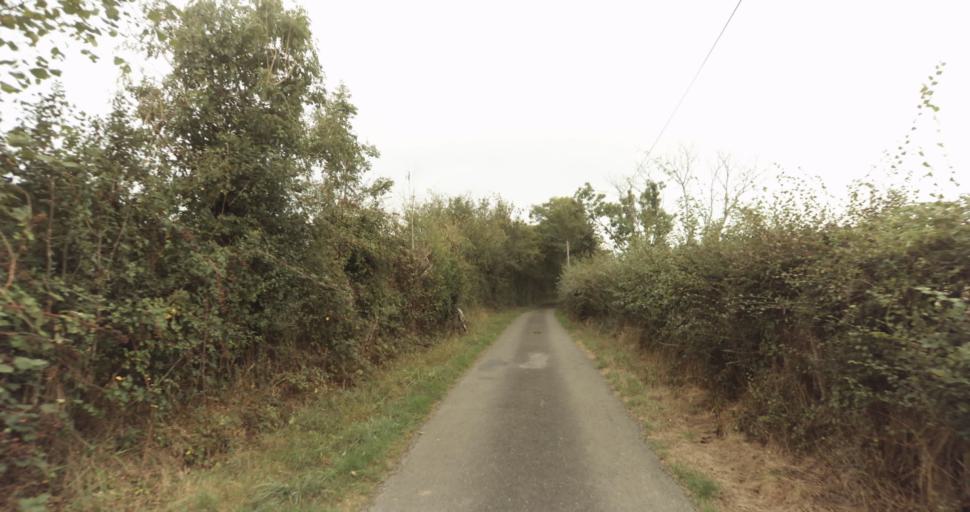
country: FR
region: Lower Normandy
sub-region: Departement de l'Orne
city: Gace
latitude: 48.8587
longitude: 0.3200
